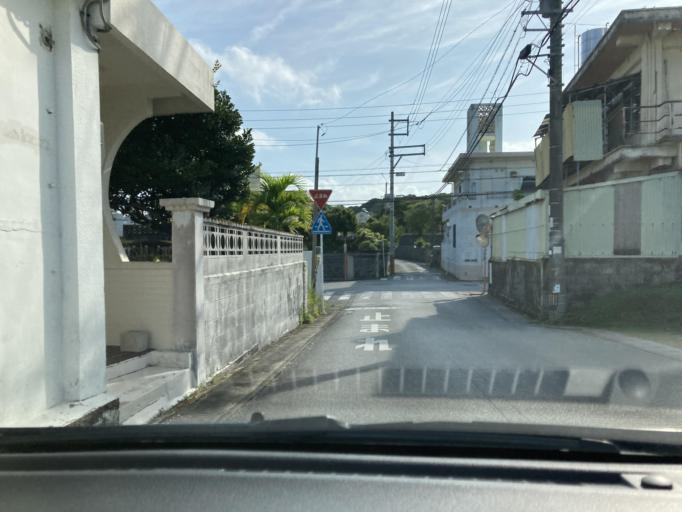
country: JP
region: Okinawa
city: Ginowan
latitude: 26.2325
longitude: 127.7434
